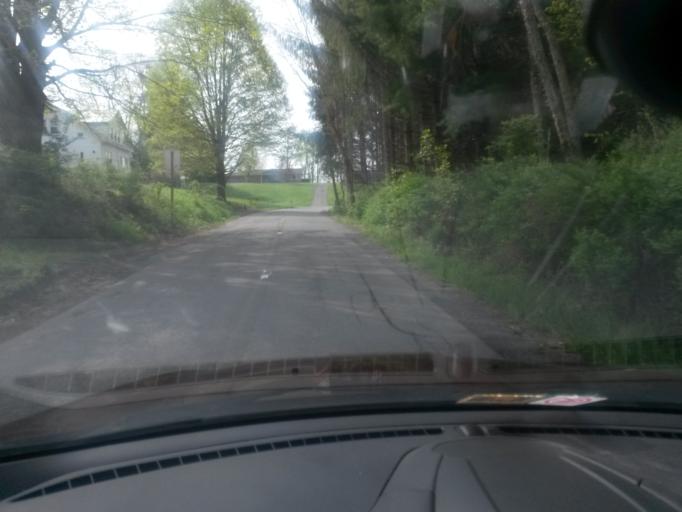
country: US
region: West Virginia
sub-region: Pocahontas County
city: Marlinton
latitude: 38.1329
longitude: -80.2103
